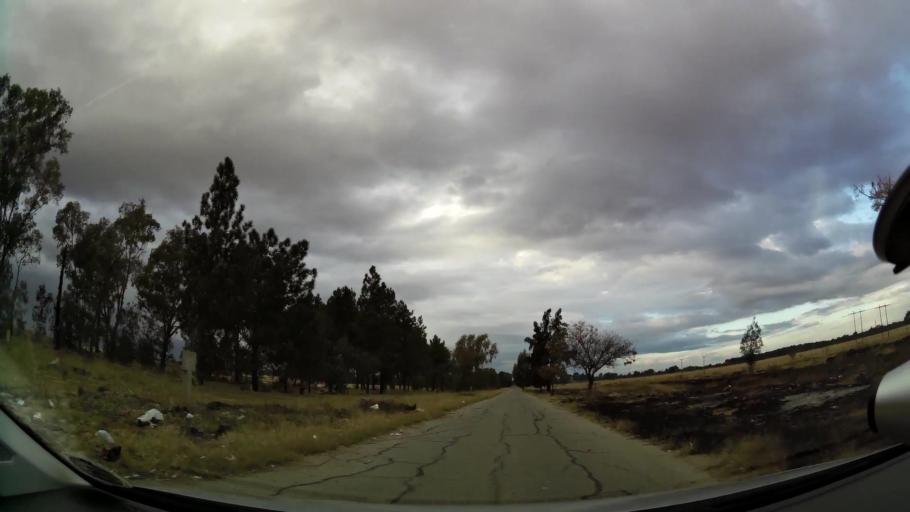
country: ZA
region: Orange Free State
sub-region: Lejweleputswa District Municipality
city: Welkom
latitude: -27.9645
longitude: 26.7038
